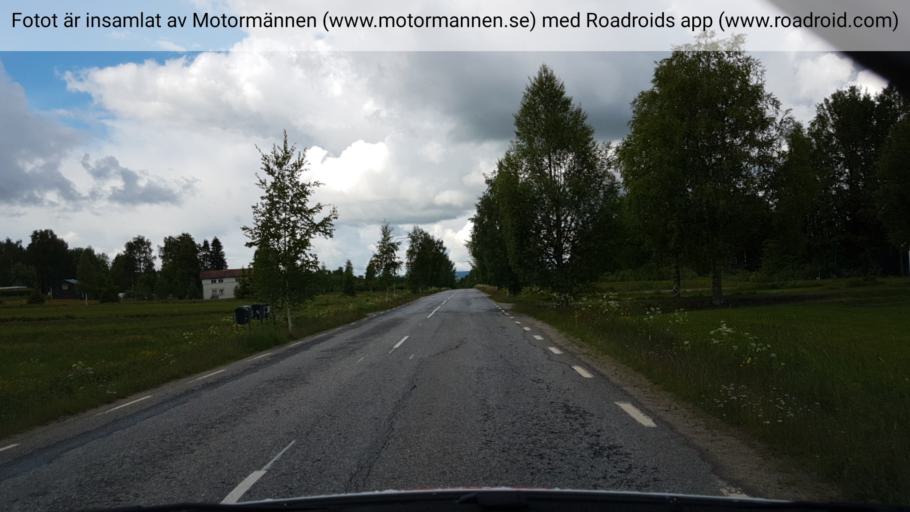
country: SE
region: Vaesterbotten
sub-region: Vannas Kommun
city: Vannasby
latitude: 63.8726
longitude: 19.8952
